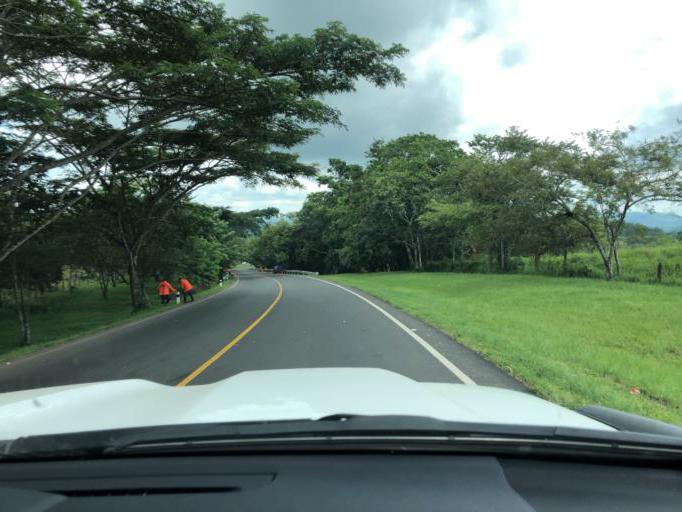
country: NI
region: Chontales
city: Santo Tomas
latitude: 12.0593
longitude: -85.0582
